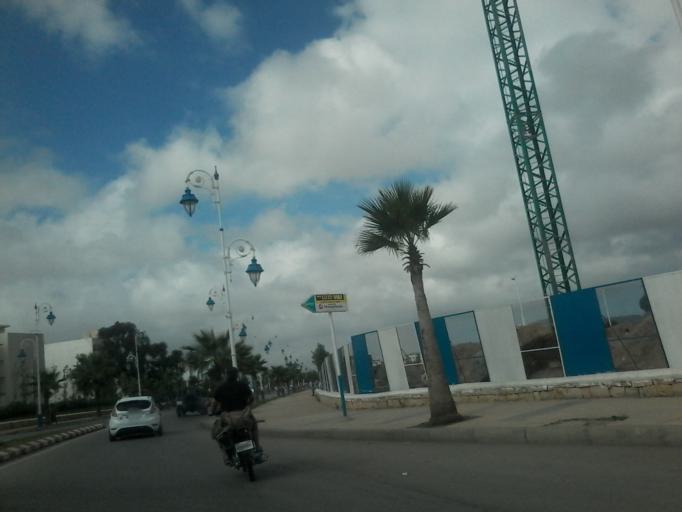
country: MA
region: Tanger-Tetouan
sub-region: Tetouan
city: Martil
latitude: 35.6278
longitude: -5.2820
